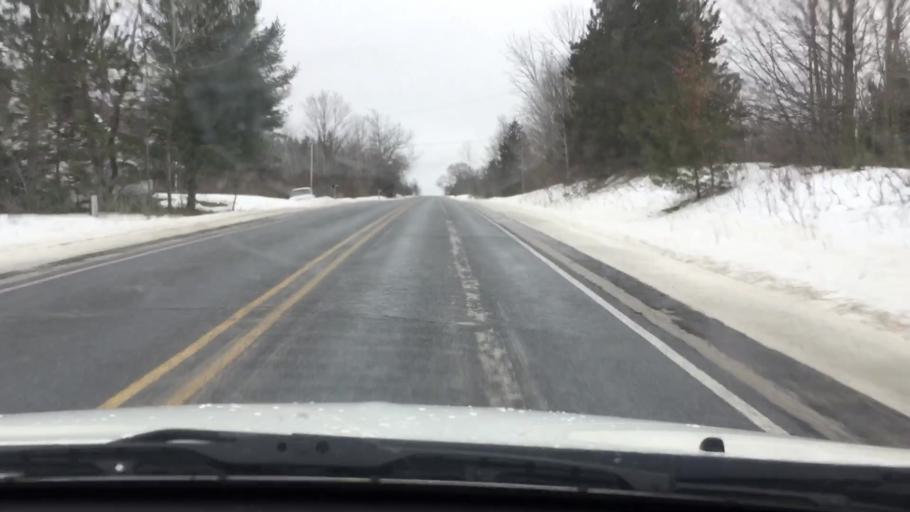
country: US
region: Michigan
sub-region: Wexford County
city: Cadillac
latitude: 44.0956
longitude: -85.4442
